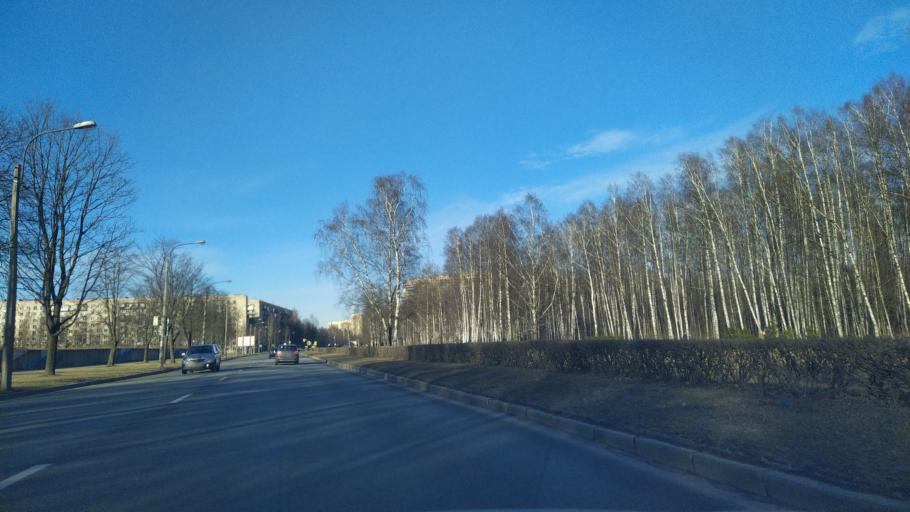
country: RU
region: Leningrad
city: Kalininskiy
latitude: 59.9973
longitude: 30.3930
